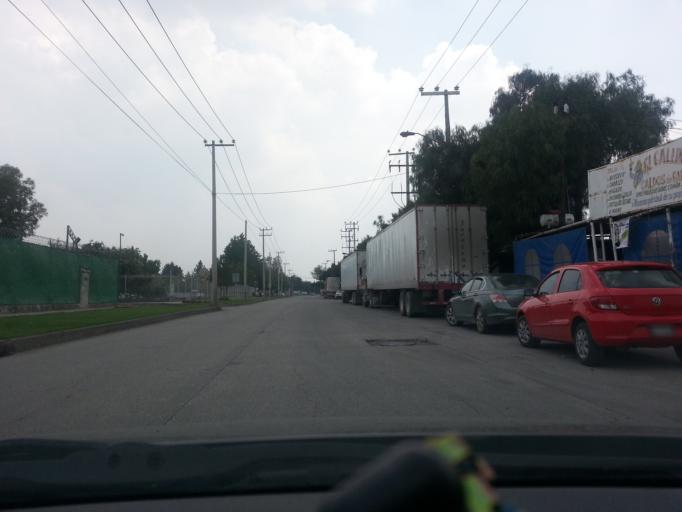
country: MX
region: Mexico
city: Cuautitlan Izcalli
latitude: 19.6616
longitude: -99.2042
